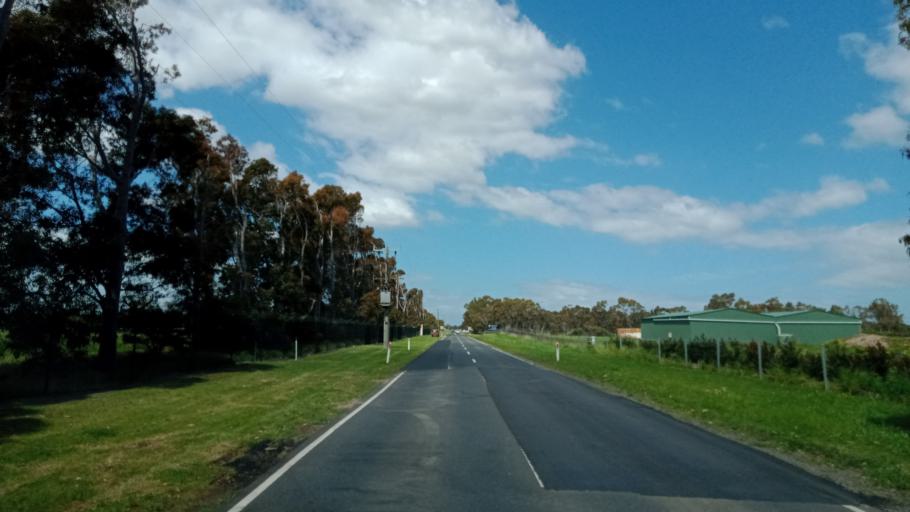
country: AU
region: Victoria
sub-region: Kingston
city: Chelsea Heights
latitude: -38.0448
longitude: 145.1481
